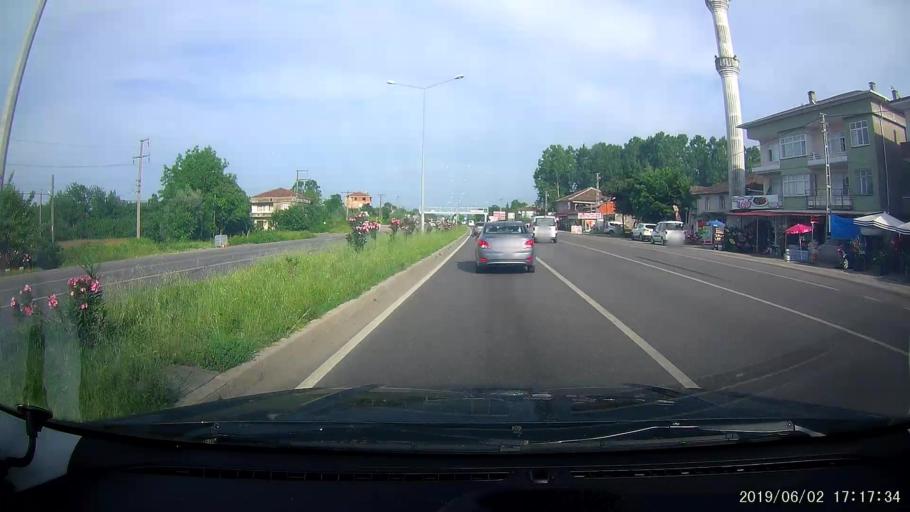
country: TR
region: Samsun
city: Dikbiyik
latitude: 41.2274
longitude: 36.5846
